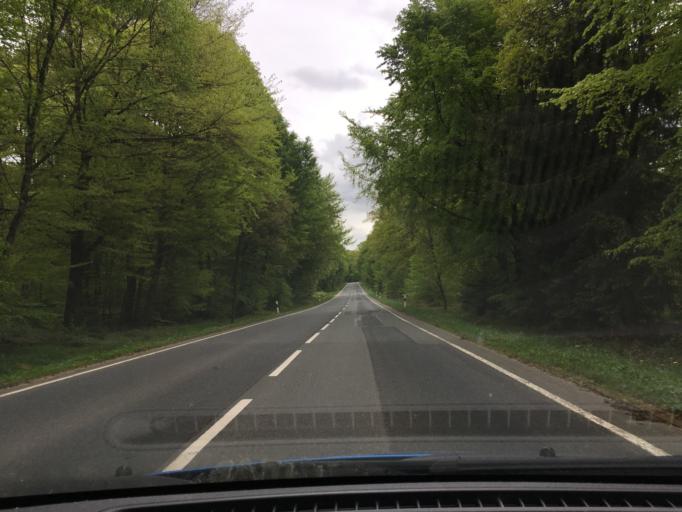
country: DE
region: Lower Saxony
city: Derental
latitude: 51.6902
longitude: 9.4880
